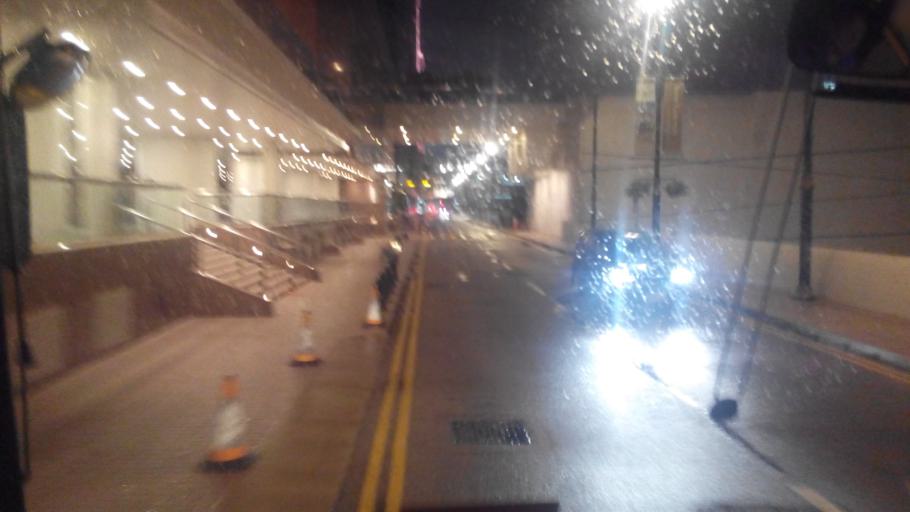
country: HK
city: Hong Kong
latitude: 22.2984
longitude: 114.1686
